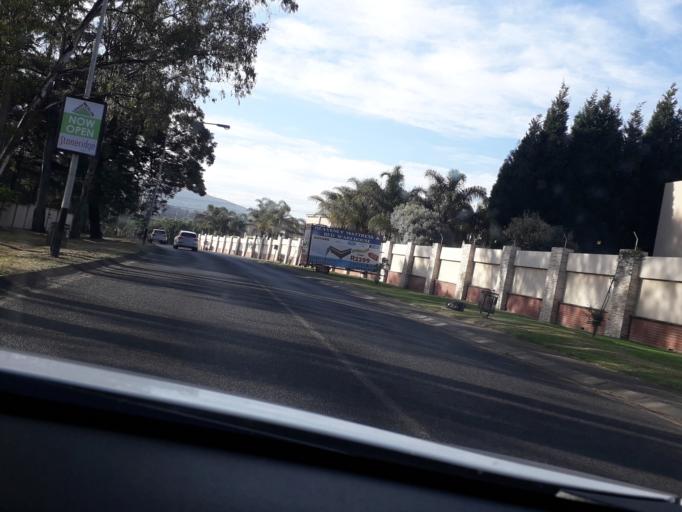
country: ZA
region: Gauteng
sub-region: City of Johannesburg Metropolitan Municipality
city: Modderfontein
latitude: -26.1594
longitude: 28.1299
